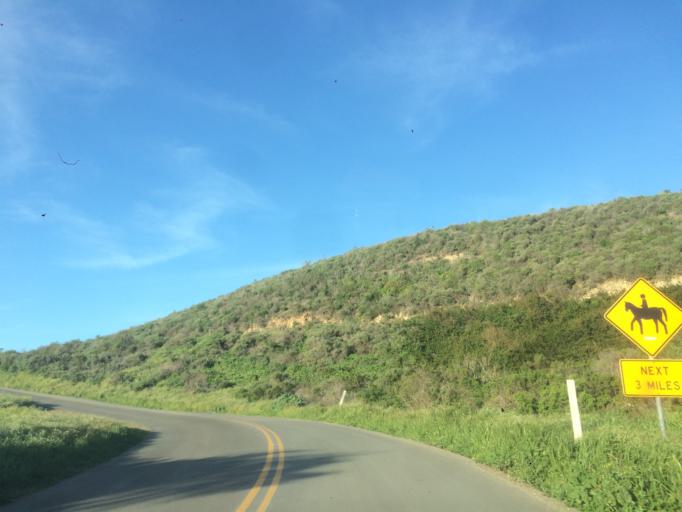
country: US
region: California
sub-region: San Luis Obispo County
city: Los Osos
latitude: 35.2750
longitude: -120.8855
